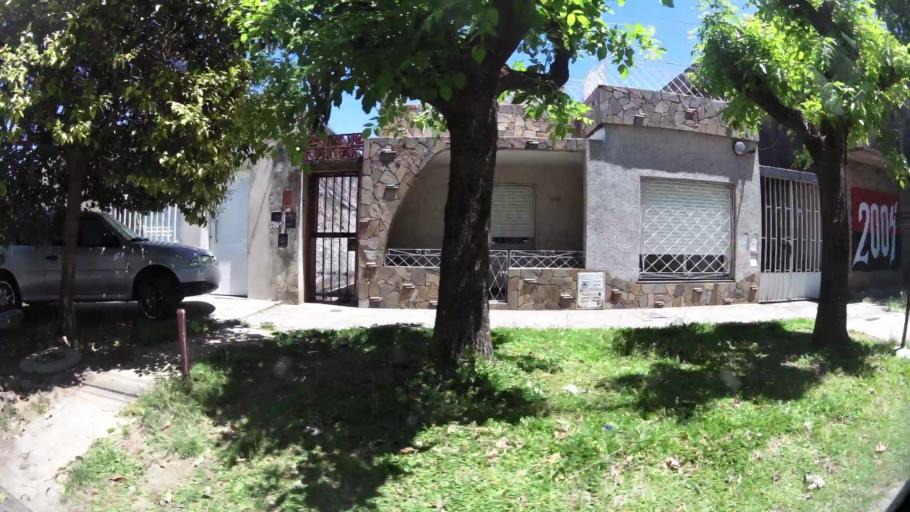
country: AR
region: Santa Fe
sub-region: Departamento de Rosario
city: Rosario
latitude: -32.9539
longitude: -60.7098
